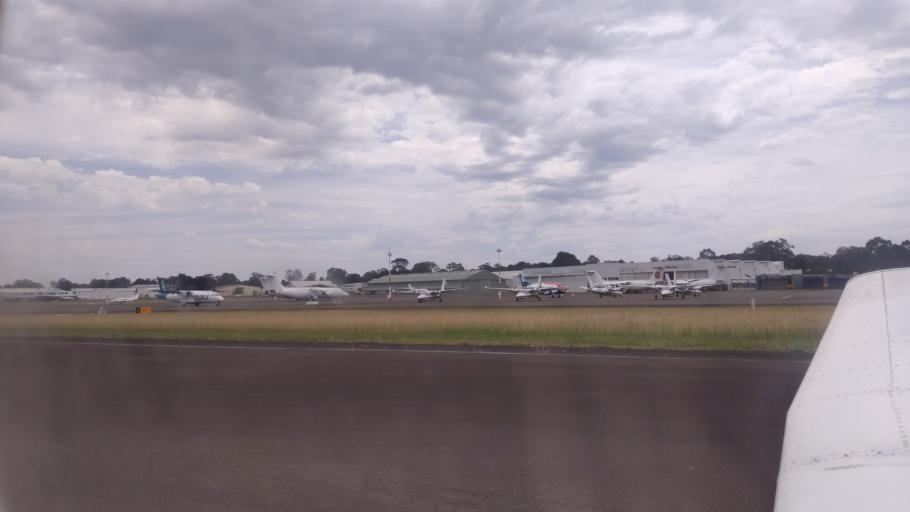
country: AU
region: New South Wales
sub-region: Bankstown
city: Milperra
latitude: -33.9217
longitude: 150.9895
